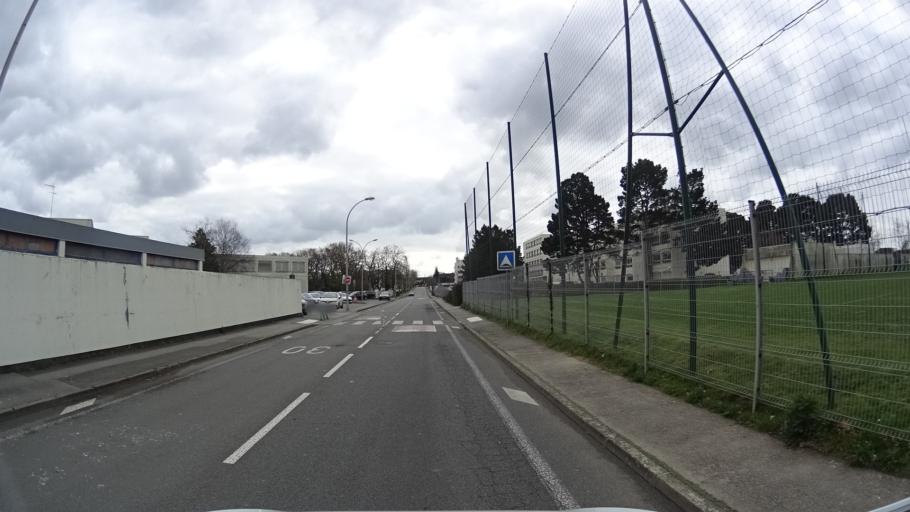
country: FR
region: Brittany
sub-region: Departement du Morbihan
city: Vannes
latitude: 47.6455
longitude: -2.7774
